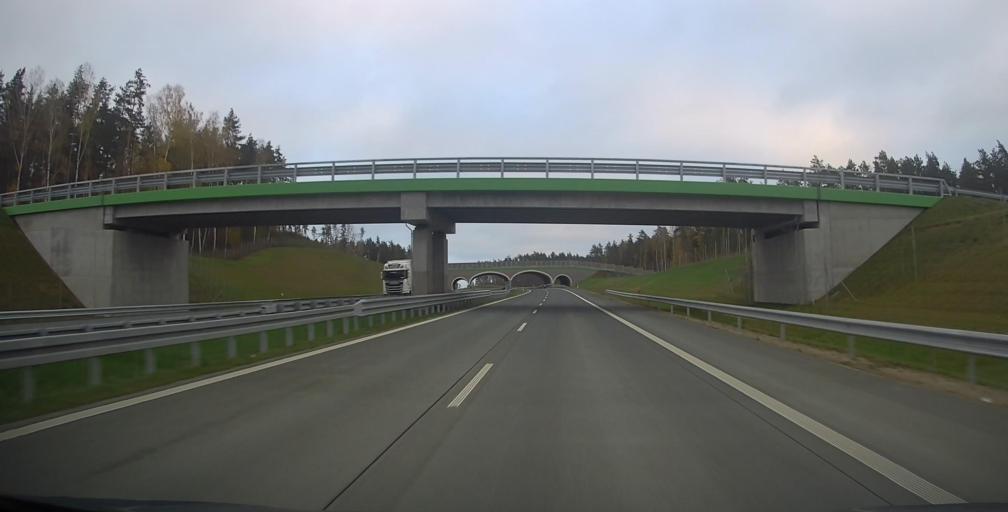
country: PL
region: Podlasie
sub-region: Powiat grajewski
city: Szczuczyn
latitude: 53.5151
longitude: 22.2529
